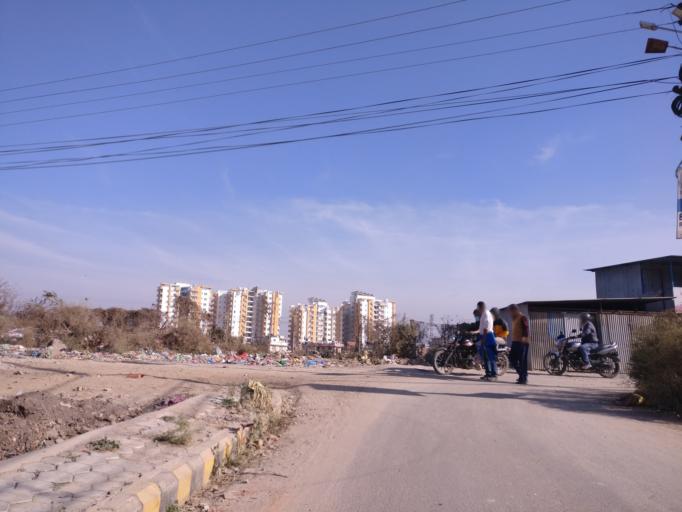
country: NP
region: Central Region
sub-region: Bagmati Zone
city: Patan
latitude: 27.6738
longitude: 85.3358
